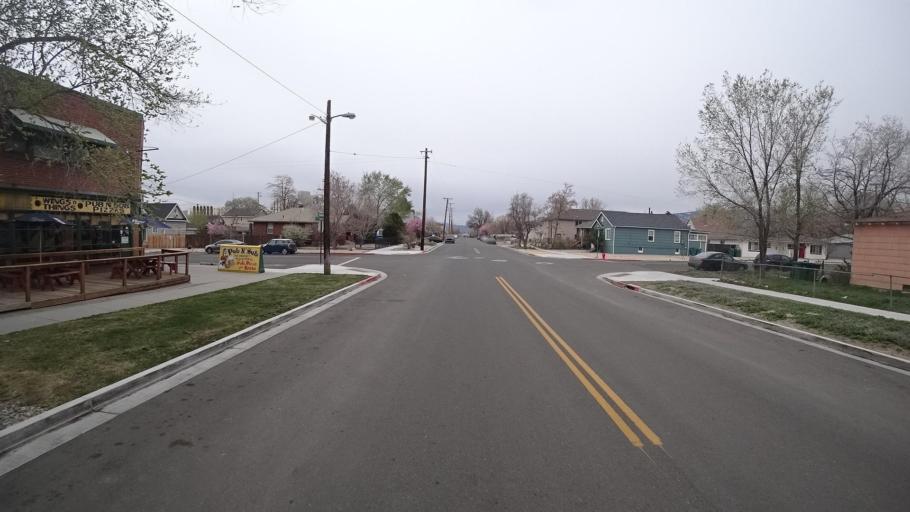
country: US
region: Nevada
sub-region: Washoe County
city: Reno
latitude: 39.5368
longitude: -119.8233
